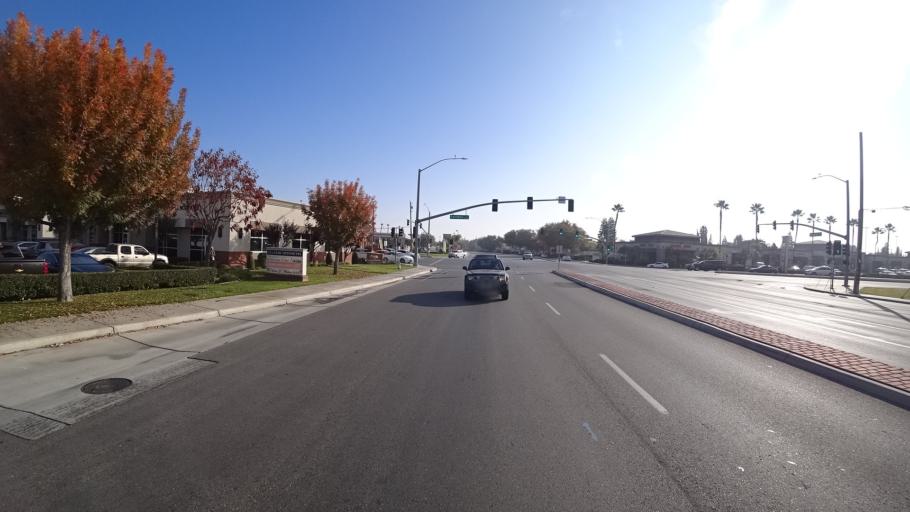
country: US
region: California
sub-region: Kern County
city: Greenacres
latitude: 35.3689
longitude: -119.1110
